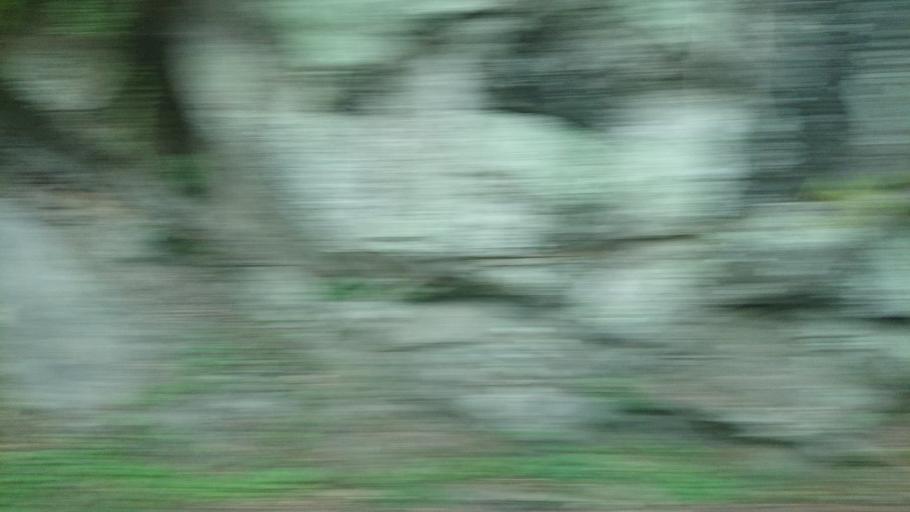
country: TW
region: Taiwan
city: Daxi
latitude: 24.8881
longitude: 121.3770
